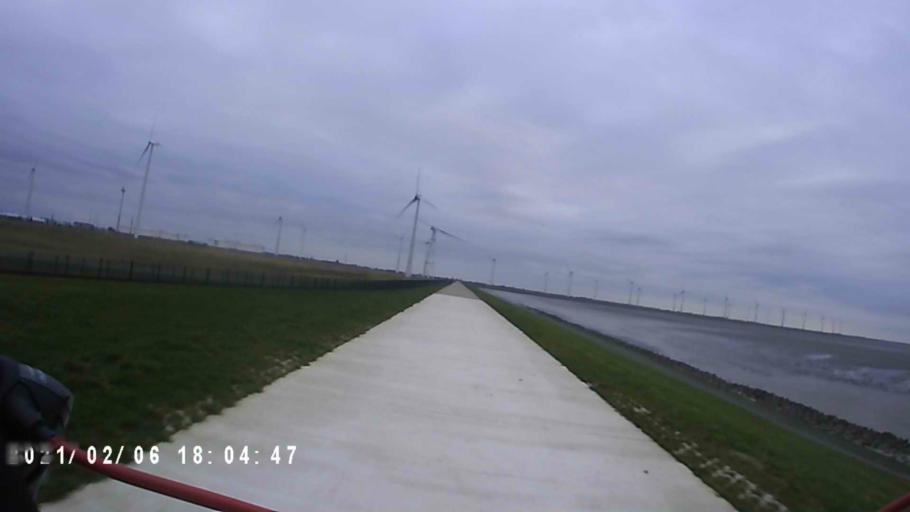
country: NL
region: Groningen
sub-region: Gemeente Appingedam
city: Appingedam
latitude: 53.4626
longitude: 6.8131
